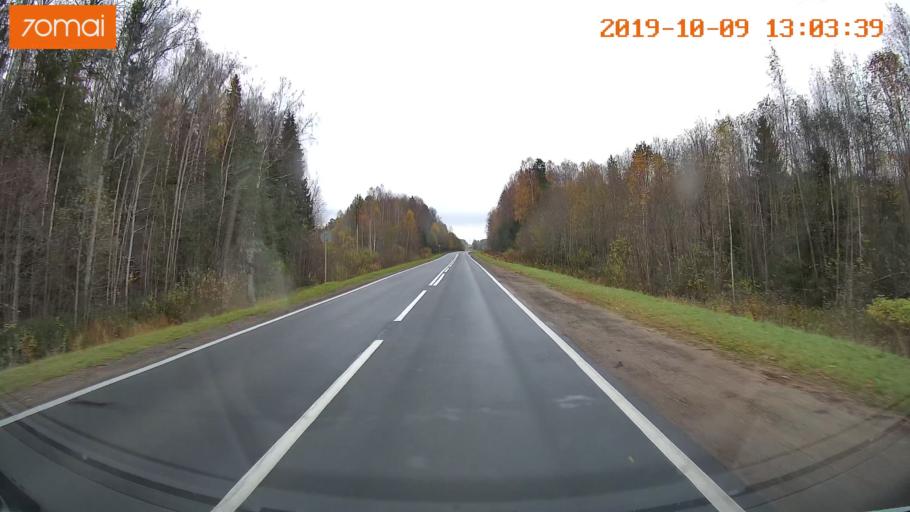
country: RU
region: Jaroslavl
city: Lyubim
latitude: 58.3592
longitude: 40.5322
